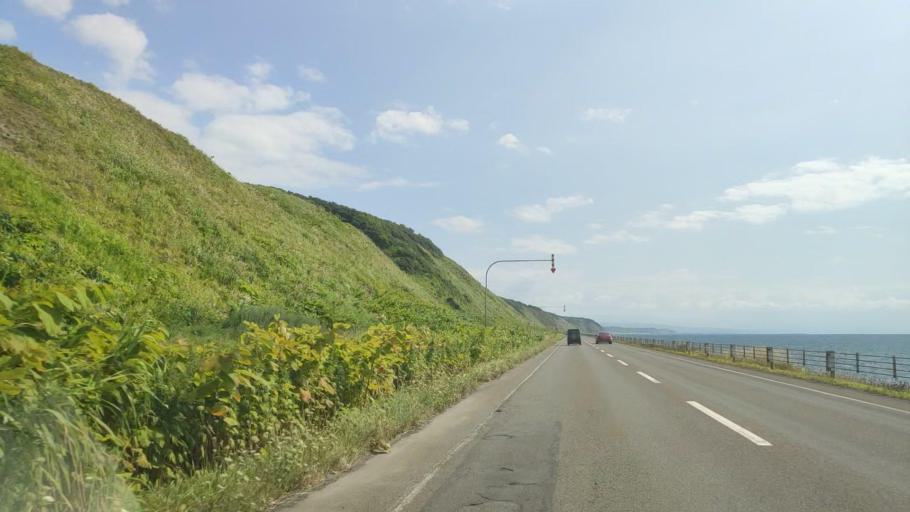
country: JP
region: Hokkaido
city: Rumoi
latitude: 44.0611
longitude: 141.6631
